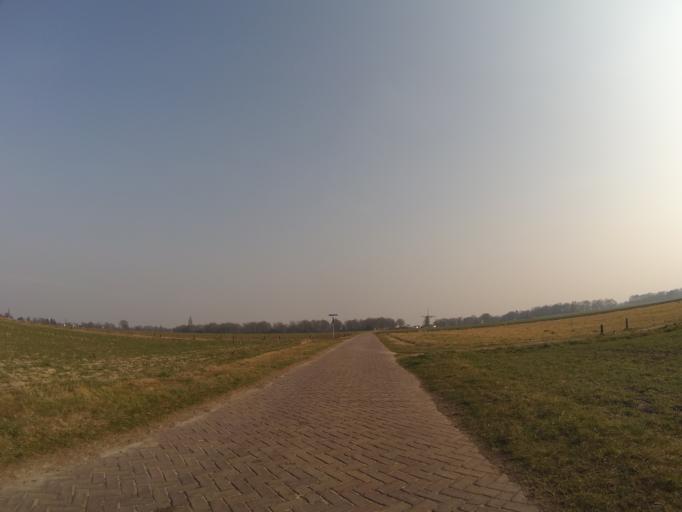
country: NL
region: Utrecht
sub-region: Gemeente Soest
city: Soest
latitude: 52.1743
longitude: 5.3010
